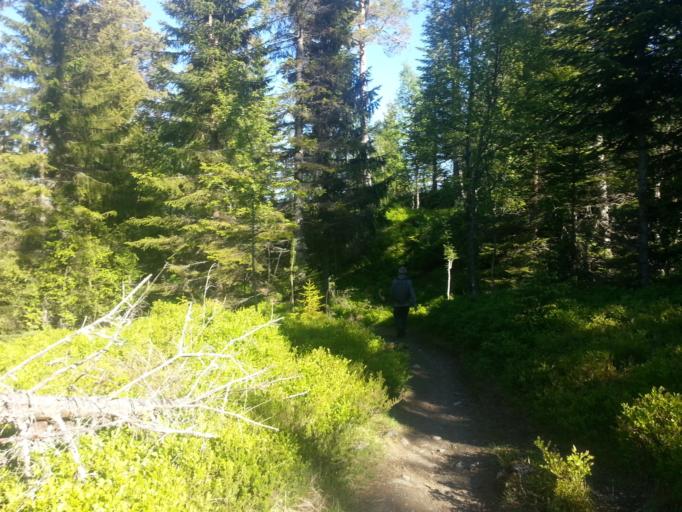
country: NO
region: Sor-Trondelag
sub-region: Trondheim
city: Trondheim
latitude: 63.4226
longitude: 10.3293
